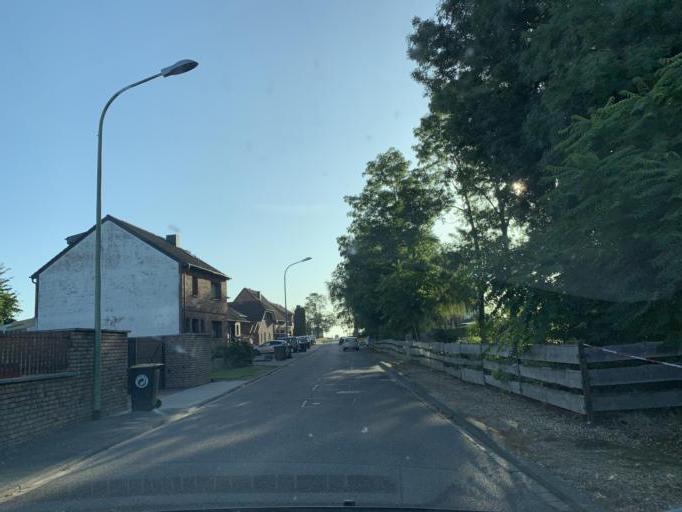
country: DE
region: North Rhine-Westphalia
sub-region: Regierungsbezirk Koln
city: Kerpen
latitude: 50.8182
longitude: 6.7010
